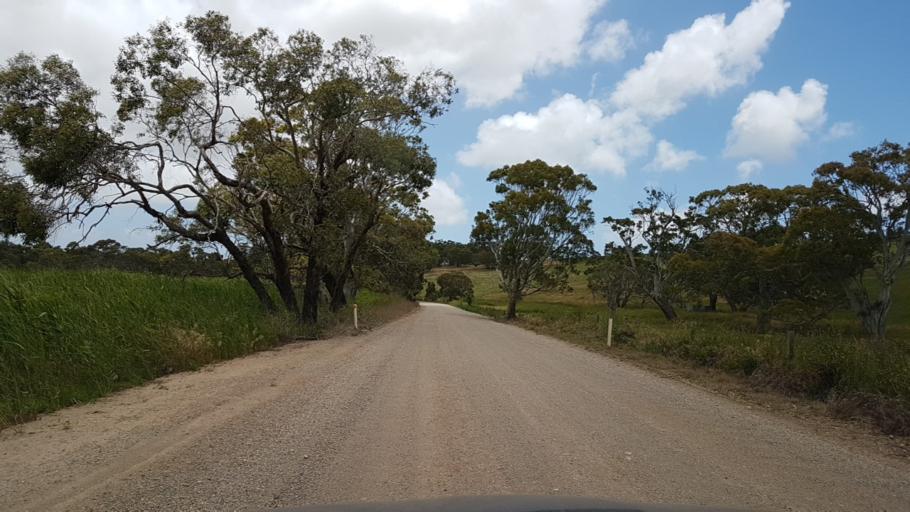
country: AU
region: South Australia
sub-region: Onkaparinga
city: Aldinga
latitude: -35.3723
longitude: 138.5167
